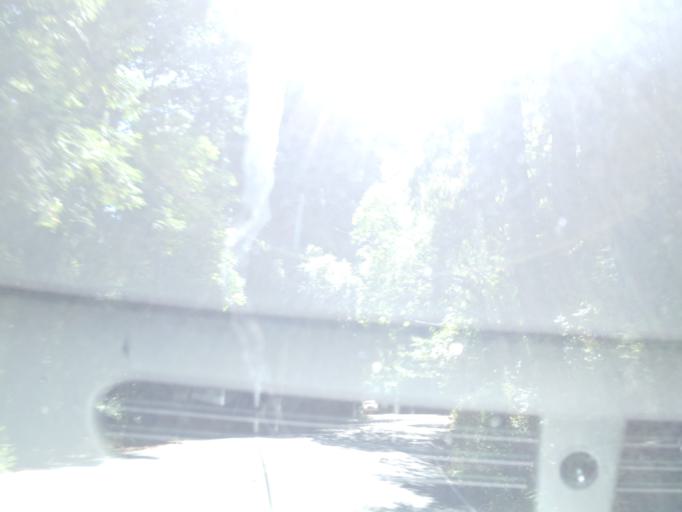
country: US
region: California
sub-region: San Mateo County
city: Portola Valley
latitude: 37.2680
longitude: -122.3222
